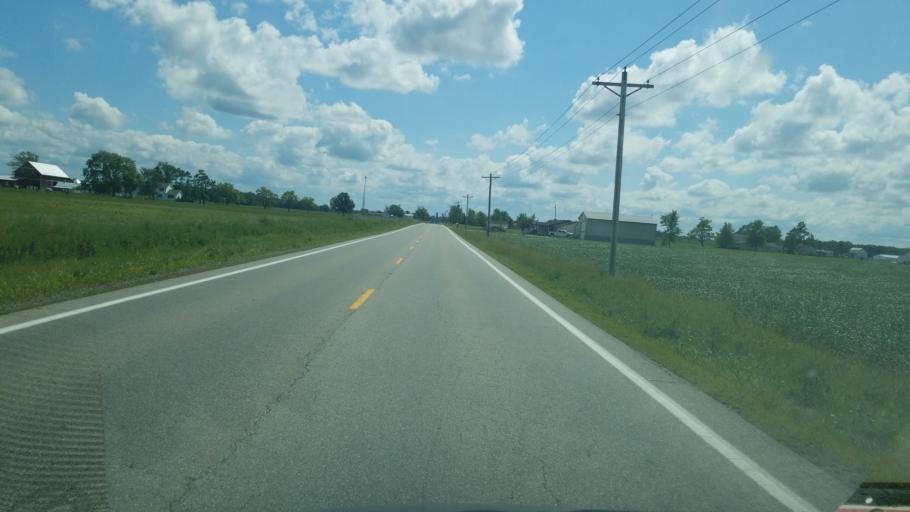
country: US
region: Ohio
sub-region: Putnam County
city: Kalida
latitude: 41.0149
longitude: -84.1980
